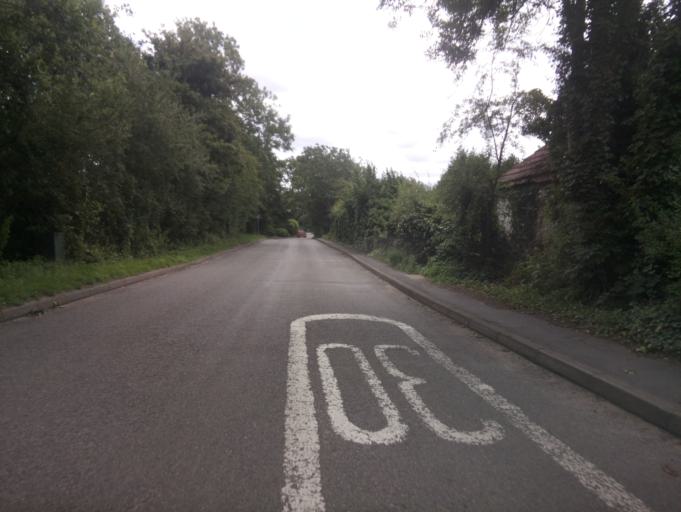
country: GB
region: England
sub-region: Nottinghamshire
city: Cotgrave
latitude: 52.8685
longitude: -1.0677
